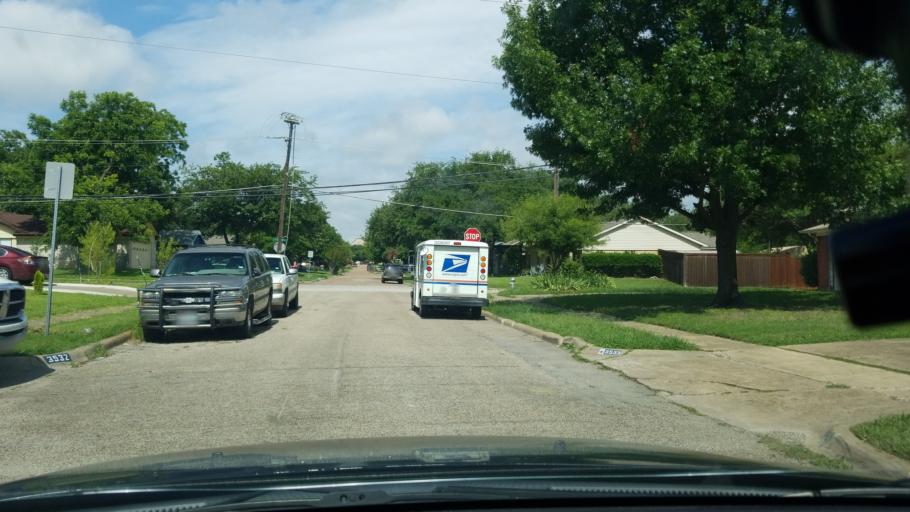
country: US
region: Texas
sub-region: Dallas County
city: Mesquite
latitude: 32.8148
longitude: -96.6529
